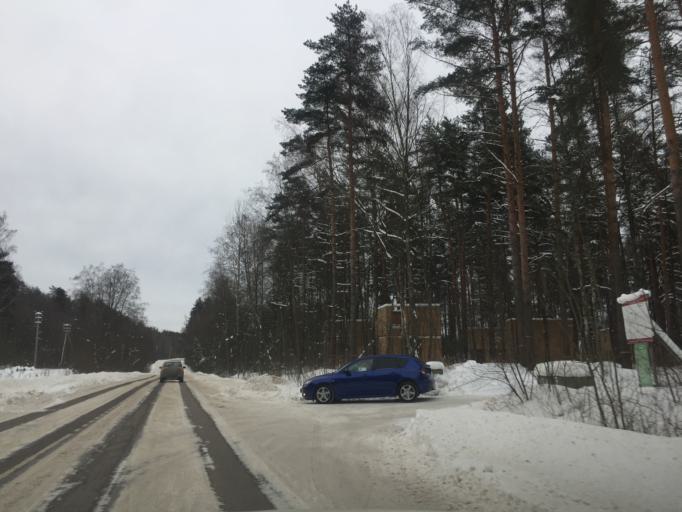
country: RU
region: Leningrad
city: Imeni Sverdlova
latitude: 59.7874
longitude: 30.7278
